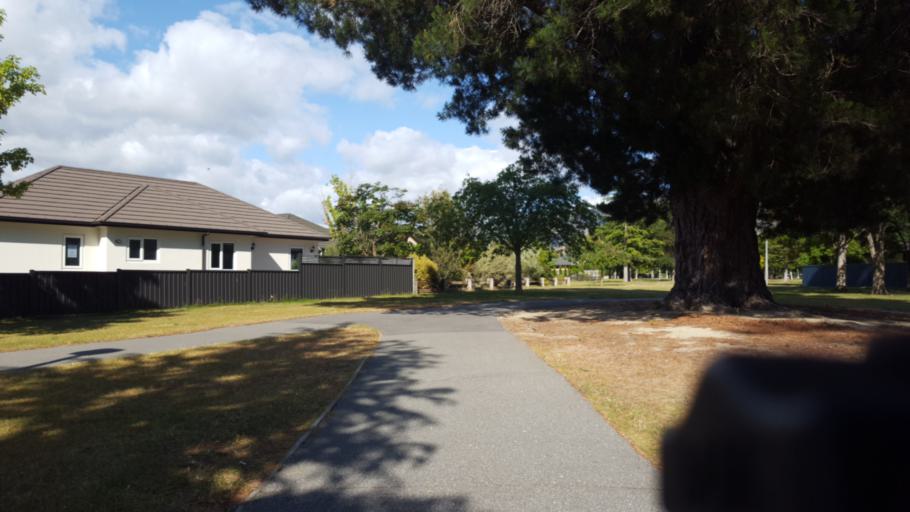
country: NZ
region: Otago
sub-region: Queenstown-Lakes District
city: Wanaka
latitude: -45.0425
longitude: 169.1915
